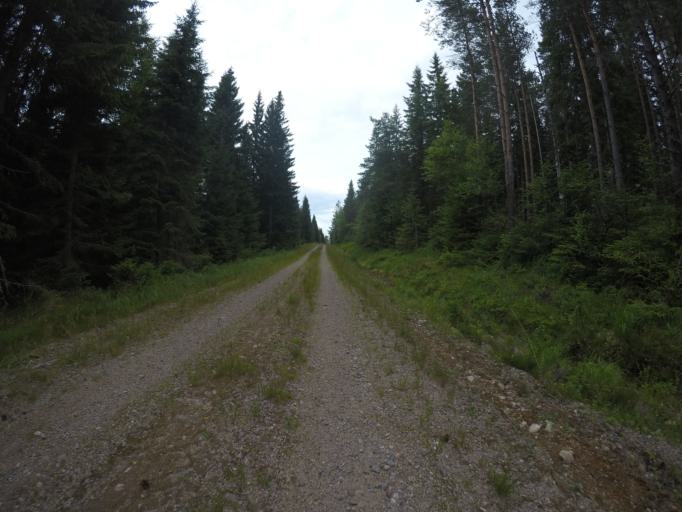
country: SE
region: Vaermland
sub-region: Filipstads Kommun
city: Lesjofors
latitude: 60.1980
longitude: 14.2556
